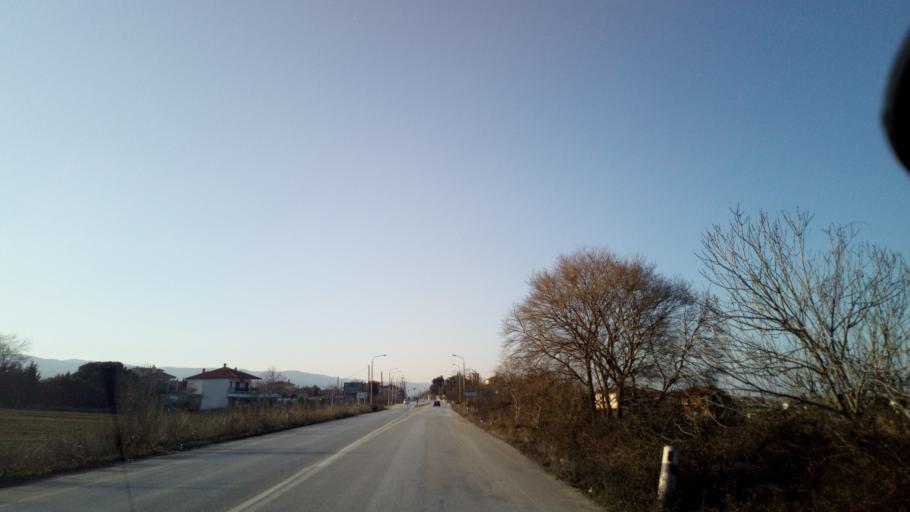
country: GR
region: Central Macedonia
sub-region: Nomos Thessalonikis
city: Agios Vasileios
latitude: 40.6623
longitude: 23.1199
